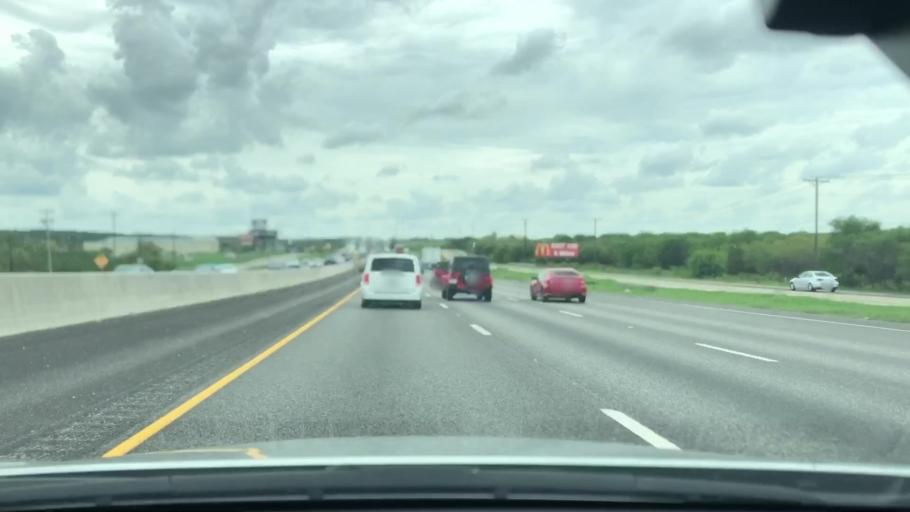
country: US
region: Texas
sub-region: Guadalupe County
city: Lake Dunlap
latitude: 29.7726
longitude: -98.0390
